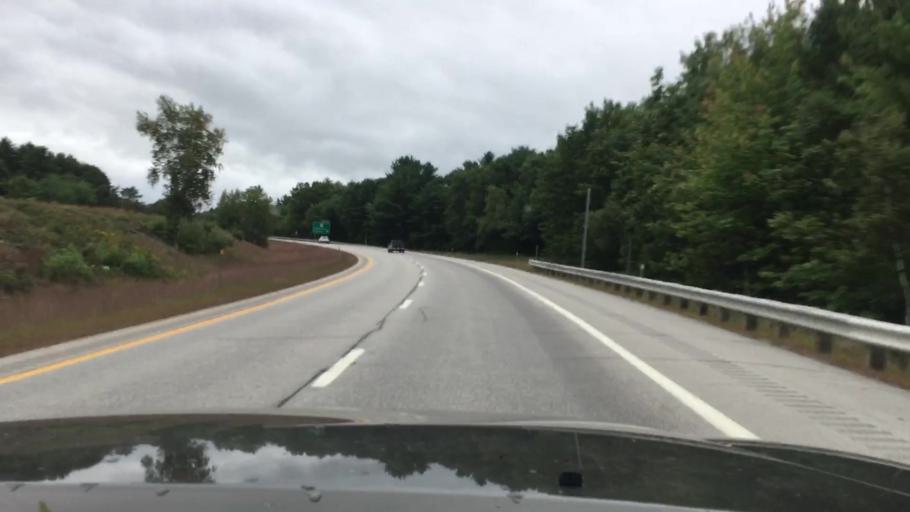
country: US
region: New Hampshire
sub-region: Belknap County
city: Sanbornton
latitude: 43.5077
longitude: -71.6179
